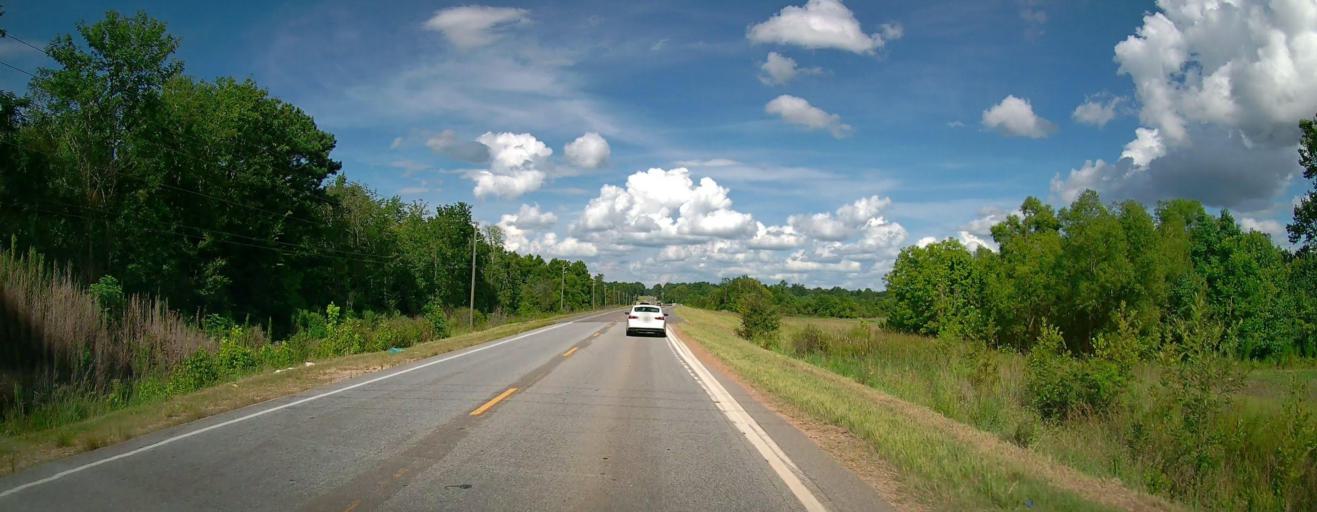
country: US
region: Alabama
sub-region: Russell County
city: Ladonia
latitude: 32.4603
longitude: -85.1426
